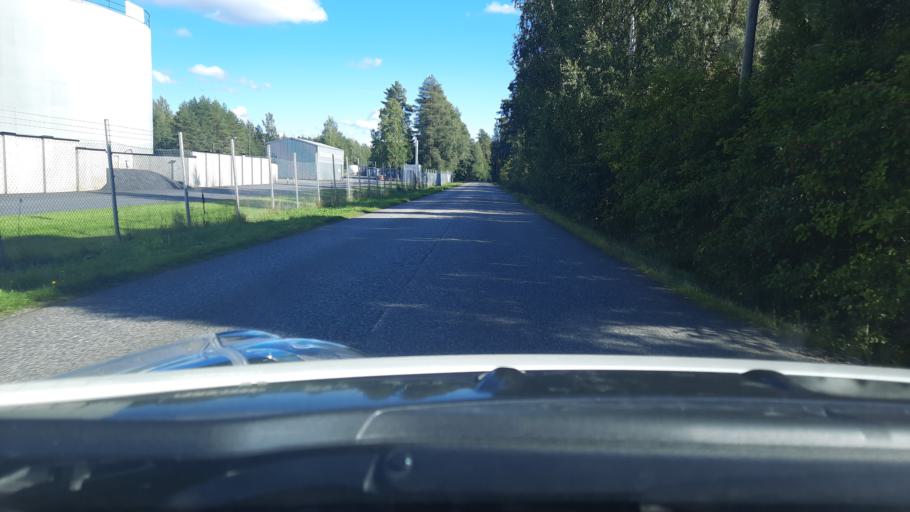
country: FI
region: North Karelia
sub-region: Joensuu
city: Joensuu
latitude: 62.6366
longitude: 29.6943
